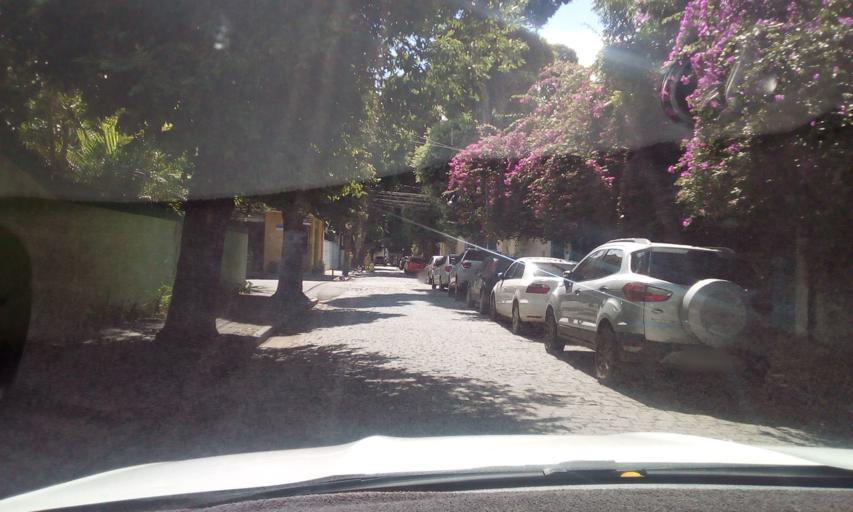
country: BR
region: Pernambuco
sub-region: Recife
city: Recife
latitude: -8.0528
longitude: -34.8891
